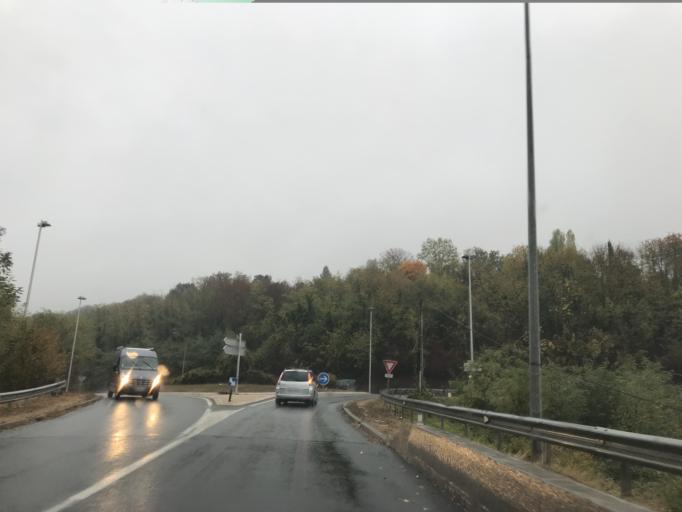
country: FR
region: Auvergne
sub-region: Departement du Puy-de-Dome
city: Dallet
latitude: 45.7742
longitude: 3.2396
